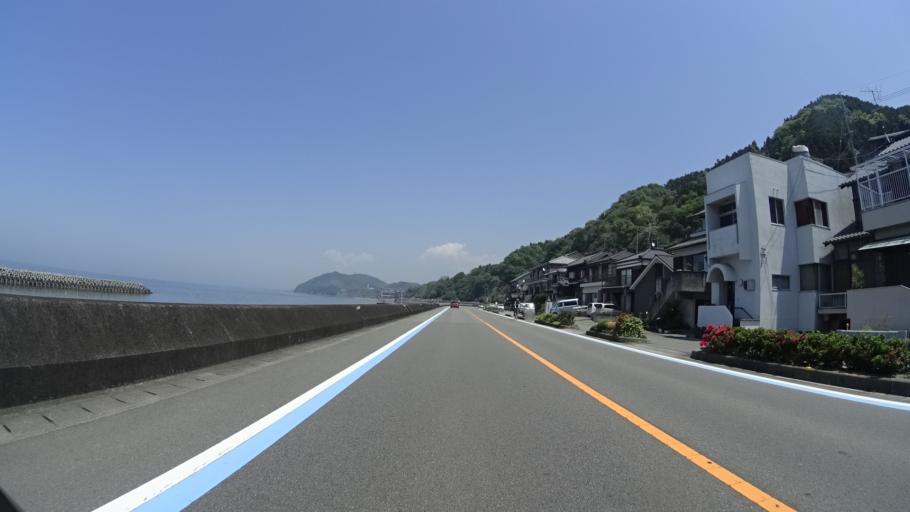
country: JP
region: Ehime
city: Iyo
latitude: 33.6952
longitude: 132.6499
